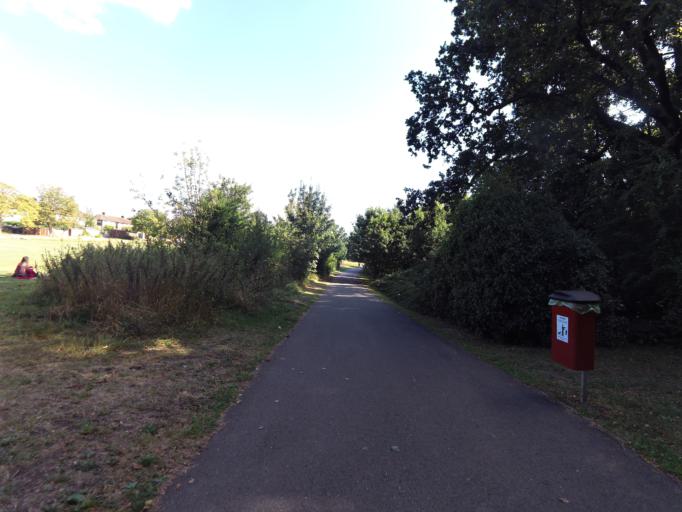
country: GB
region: England
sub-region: Greater London
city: Wood Green
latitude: 51.6312
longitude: -0.1445
